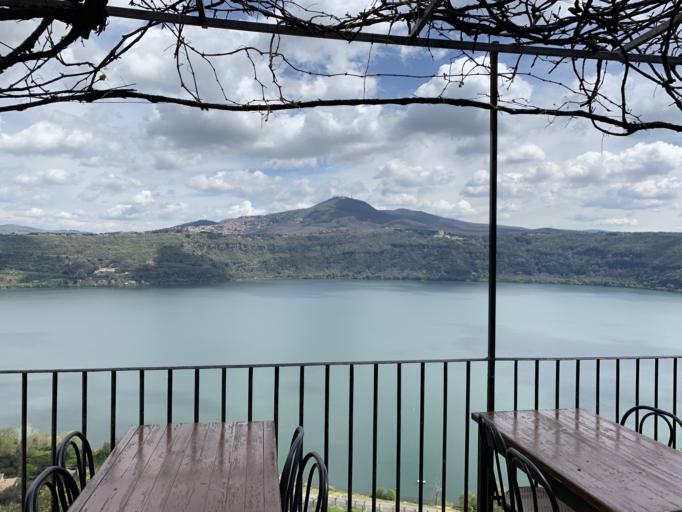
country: IT
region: Latium
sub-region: Citta metropolitana di Roma Capitale
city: Castel Gandolfo
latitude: 41.7453
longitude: 12.6513
